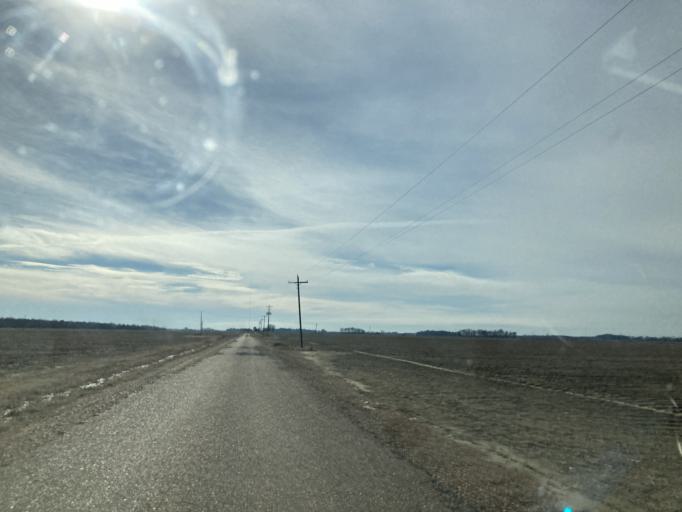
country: US
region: Mississippi
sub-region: Humphreys County
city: Belzoni
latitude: 33.0659
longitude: -90.6339
